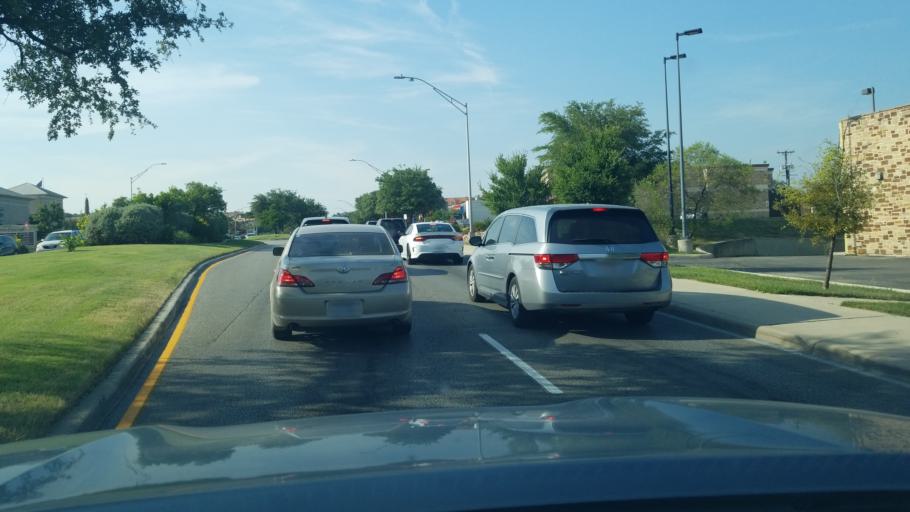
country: US
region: Texas
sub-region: Bexar County
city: Hollywood Park
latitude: 29.6243
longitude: -98.4947
